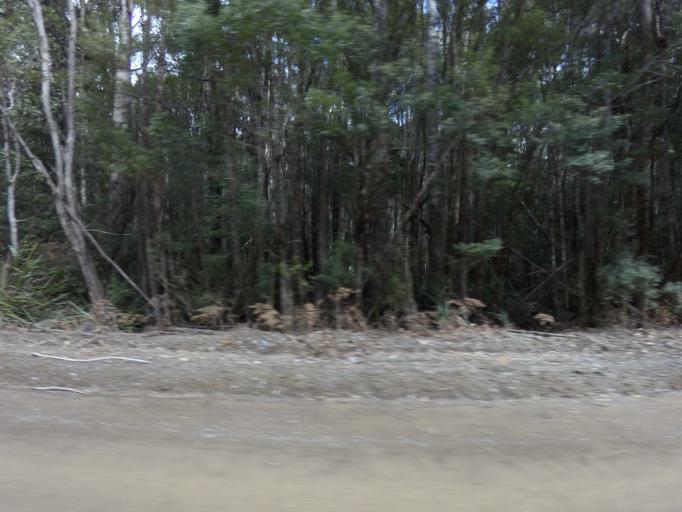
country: AU
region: Tasmania
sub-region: Huon Valley
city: Geeveston
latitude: -43.3964
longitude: 146.8595
